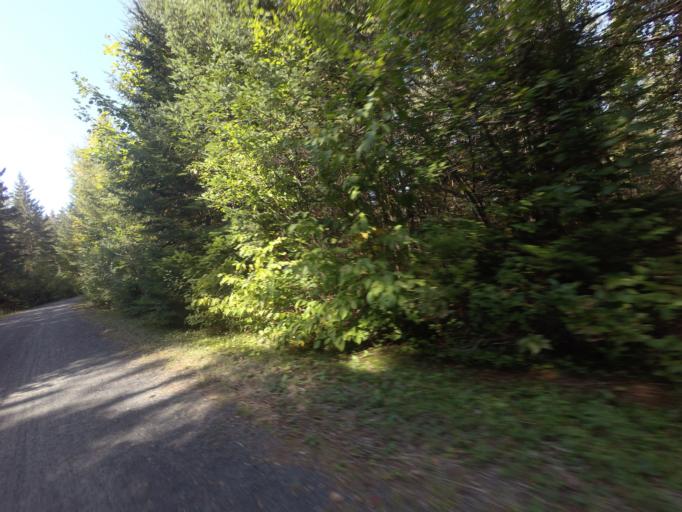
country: CA
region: Quebec
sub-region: Laurentides
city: Sainte-Agathe-des-Monts
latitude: 46.0598
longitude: -74.2915
